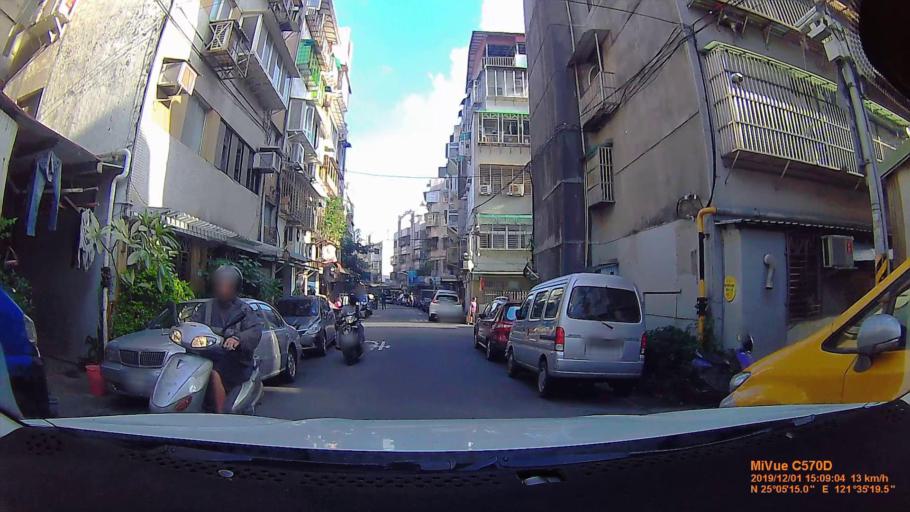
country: TW
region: Taipei
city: Taipei
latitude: 25.0876
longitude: 121.5887
